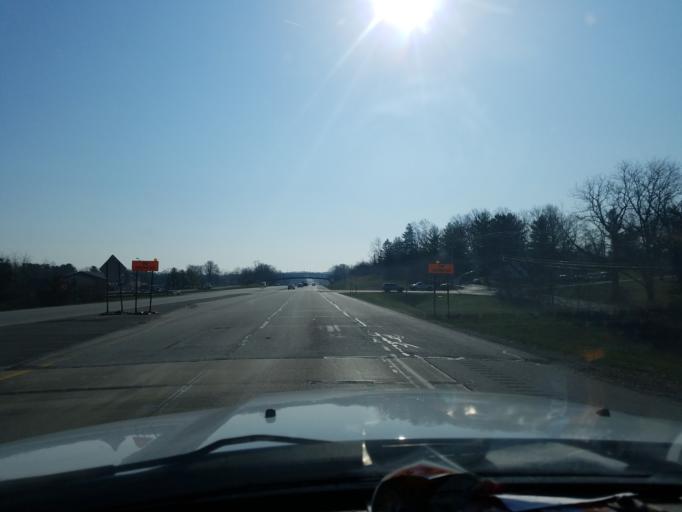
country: US
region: Indiana
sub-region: Monroe County
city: Bloomington
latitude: 39.1868
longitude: -86.5481
